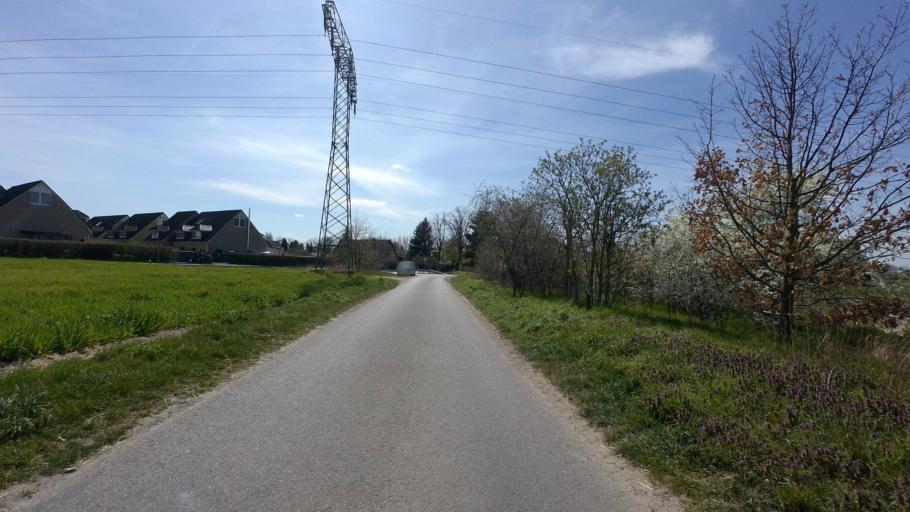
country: DE
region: Brandenburg
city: Schonefeld
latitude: 52.3447
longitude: 13.5199
